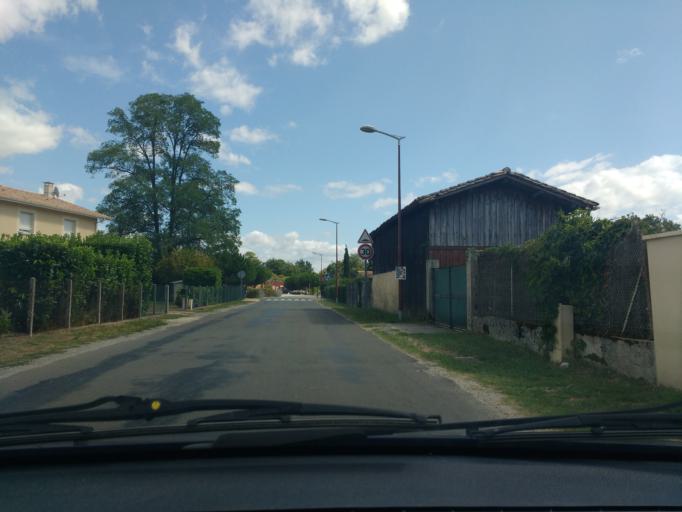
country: FR
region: Aquitaine
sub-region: Departement de la Gironde
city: Salles
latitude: 44.5492
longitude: -0.8646
